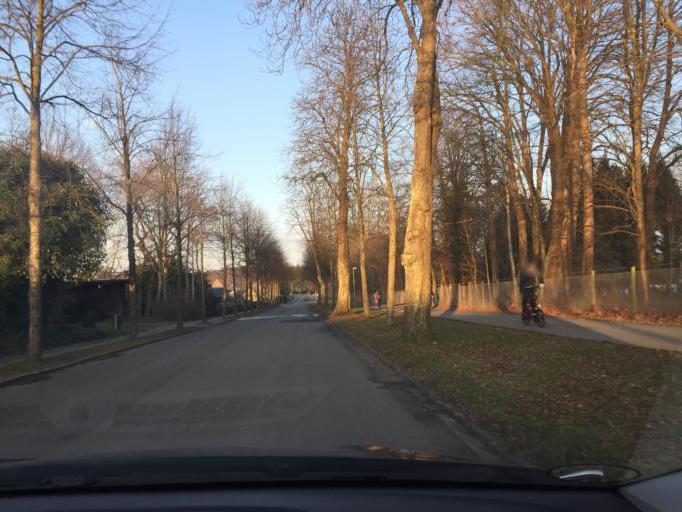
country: DK
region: South Denmark
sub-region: Odense Kommune
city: Odense
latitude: 55.3634
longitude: 10.3702
